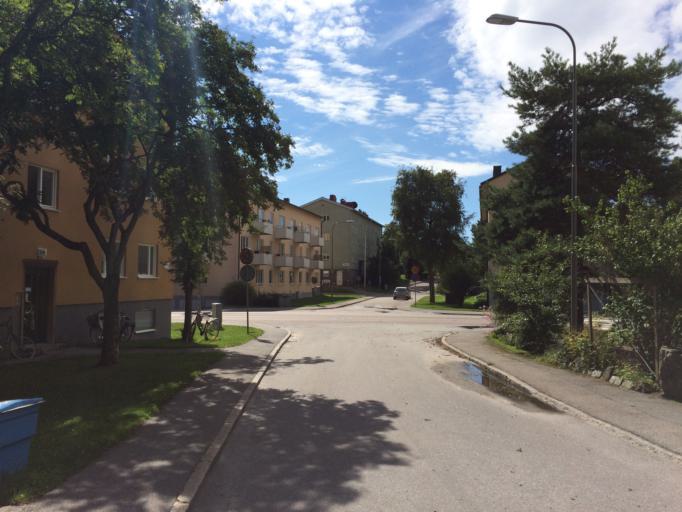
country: SE
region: Stockholm
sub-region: Solna Kommun
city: Solna
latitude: 59.3019
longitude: 17.9894
